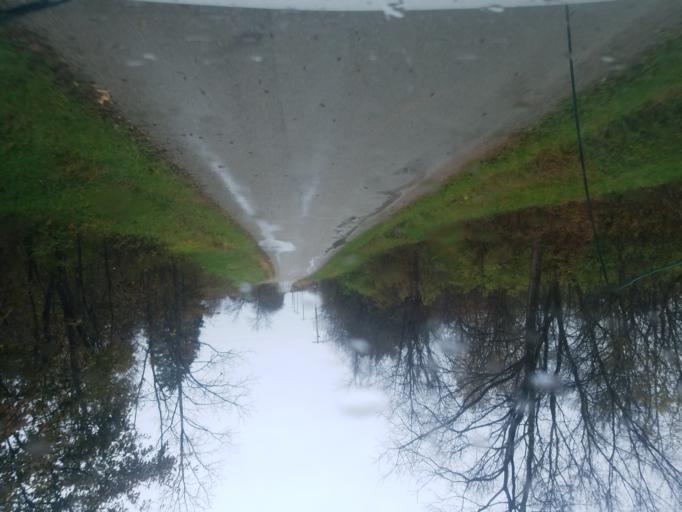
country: US
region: Ohio
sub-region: Washington County
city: Beverly
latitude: 39.4714
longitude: -81.6997
